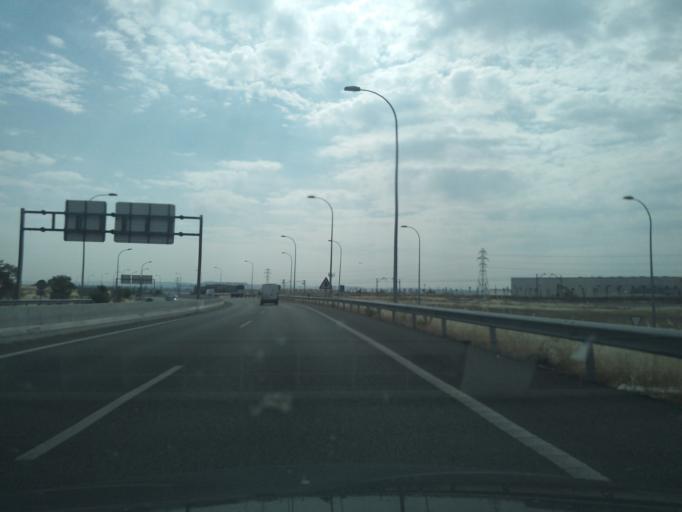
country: ES
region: Madrid
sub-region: Provincia de Madrid
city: Coslada
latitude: 40.4396
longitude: -3.5598
